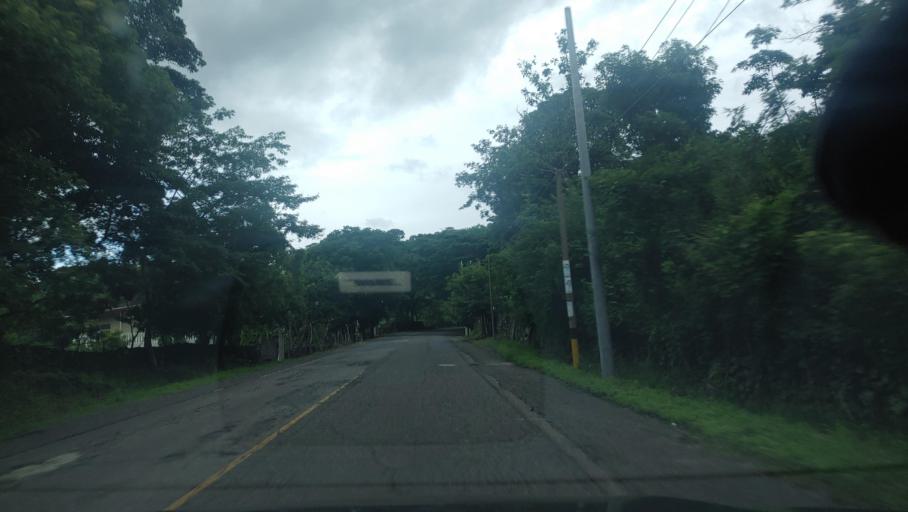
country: HN
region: Choluteca
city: Corpus
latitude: 13.3678
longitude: -87.0259
